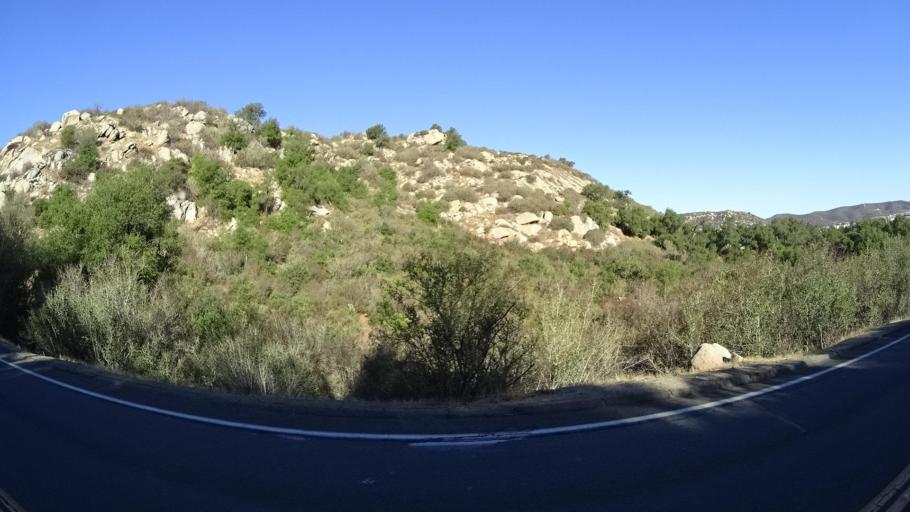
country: US
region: California
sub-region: San Diego County
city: Lakeside
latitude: 32.9274
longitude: -116.8735
